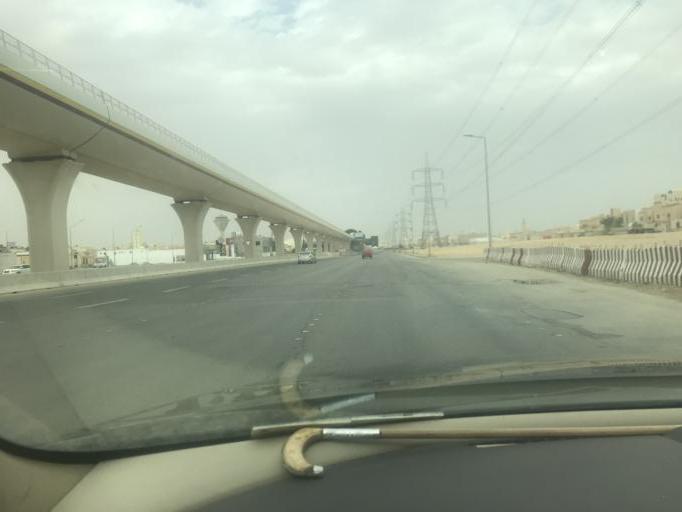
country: SA
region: Ar Riyad
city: Riyadh
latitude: 24.7987
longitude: 46.6902
